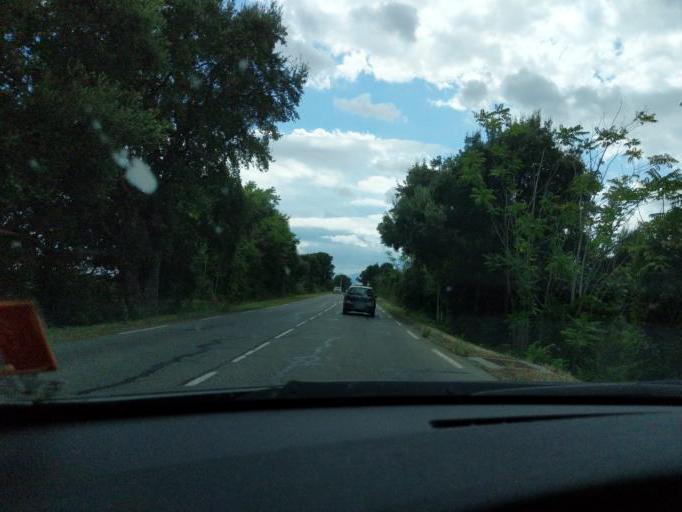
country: FR
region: Corsica
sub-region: Departement de la Haute-Corse
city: Ghisonaccia
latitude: 42.0409
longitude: 9.4232
